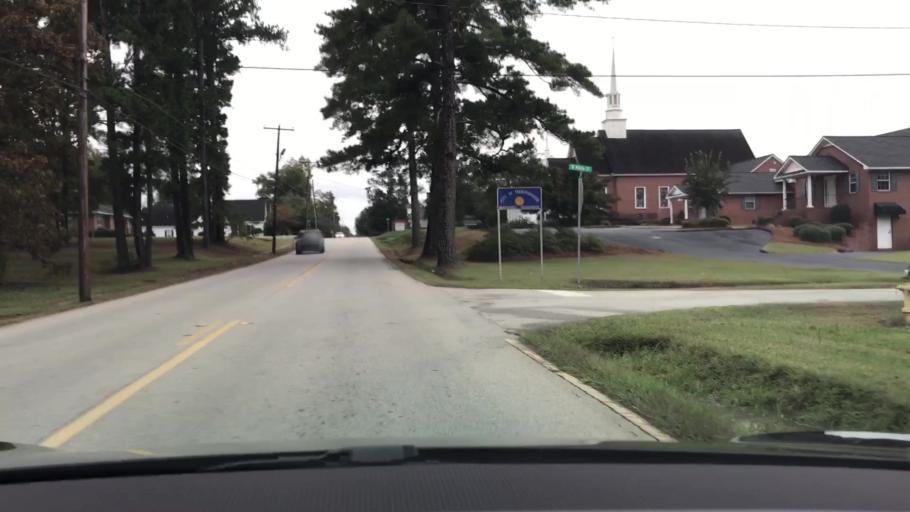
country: US
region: Georgia
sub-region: Jefferson County
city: Wrens
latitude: 33.2136
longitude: -82.4686
